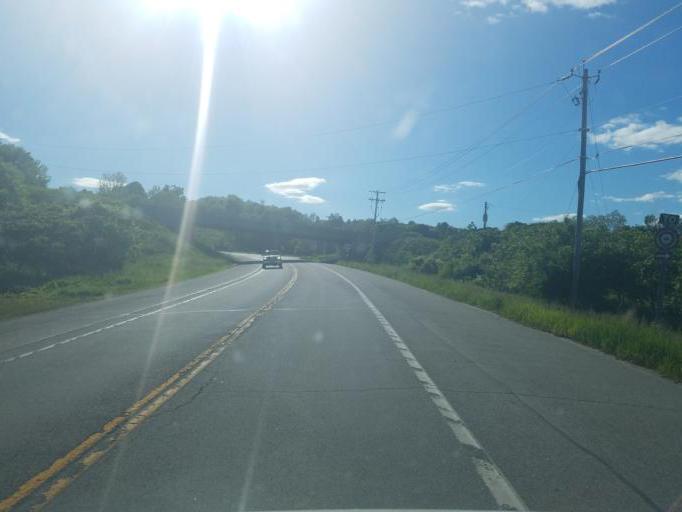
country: US
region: New York
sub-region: Herkimer County
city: Little Falls
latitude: 43.0209
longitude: -74.8175
